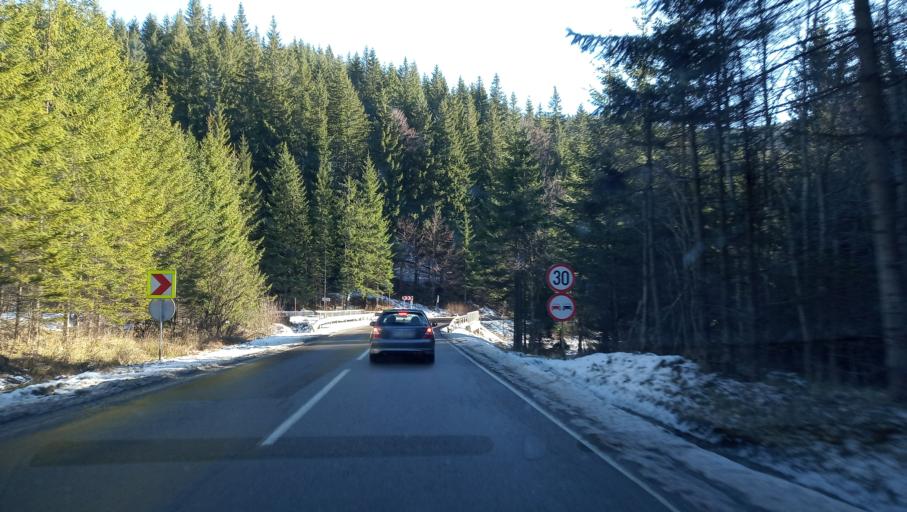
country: RO
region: Brasov
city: Crivina
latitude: 45.4825
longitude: 25.9195
